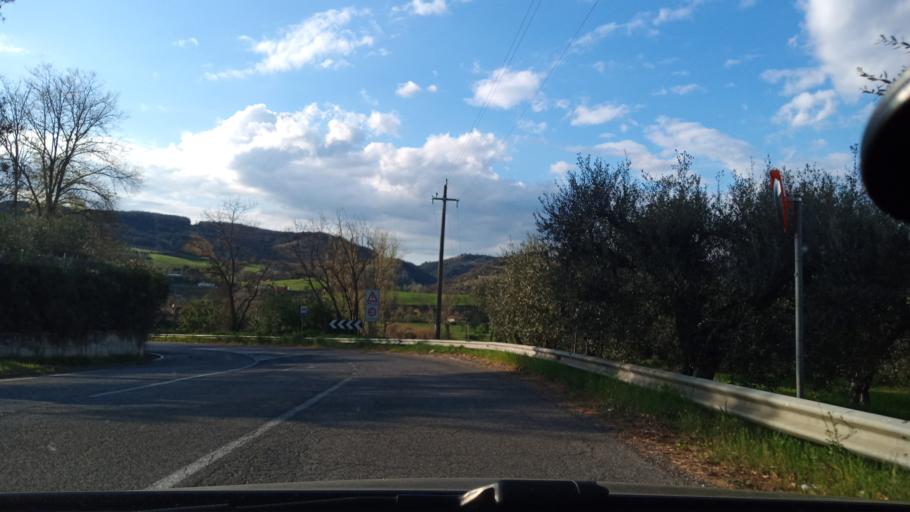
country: IT
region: Latium
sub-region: Citta metropolitana di Roma Capitale
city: Fiano Romano
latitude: 42.1788
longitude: 12.6100
